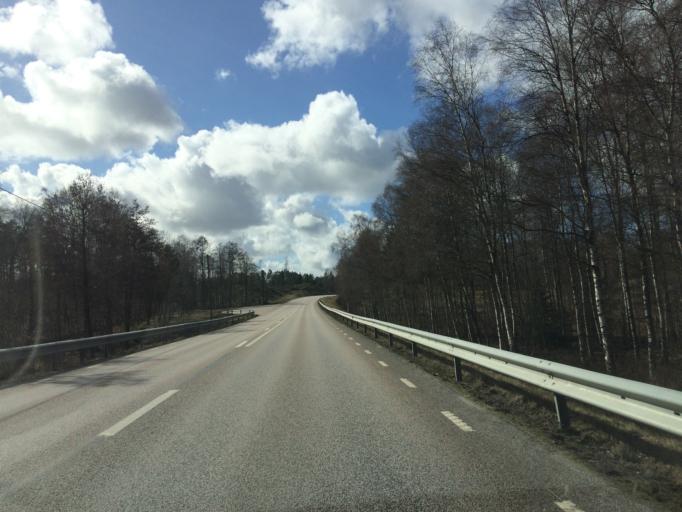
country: SE
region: Halland
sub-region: Laholms Kommun
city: Knared
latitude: 56.4895
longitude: 13.4297
